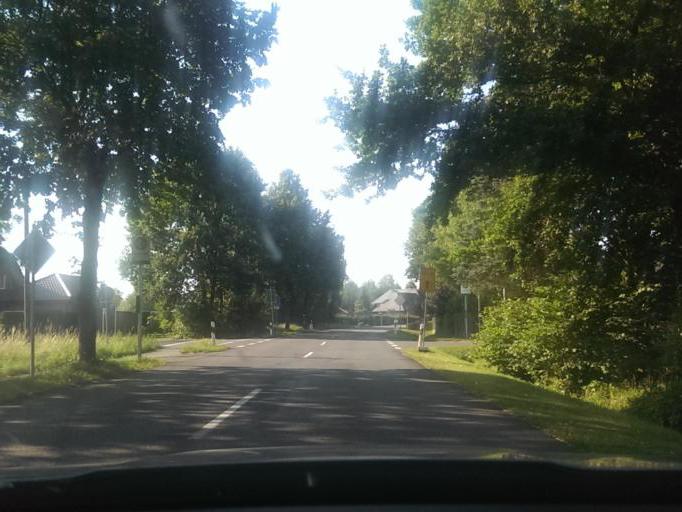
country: DE
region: North Rhine-Westphalia
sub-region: Regierungsbezirk Detmold
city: Delbruck
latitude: 51.7564
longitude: 8.5738
